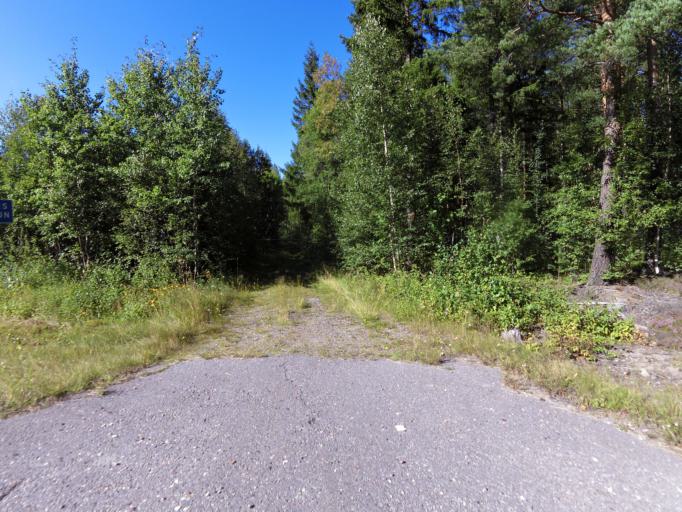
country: SE
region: Gaevleborg
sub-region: Hofors Kommun
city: Hofors
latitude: 60.5690
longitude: 16.4668
